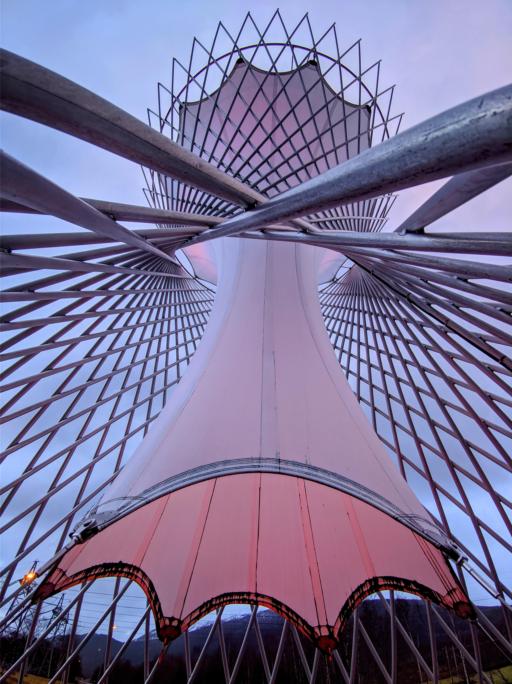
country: NO
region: Hordaland
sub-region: Etne
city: Etne
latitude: 59.8610
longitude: 5.7676
